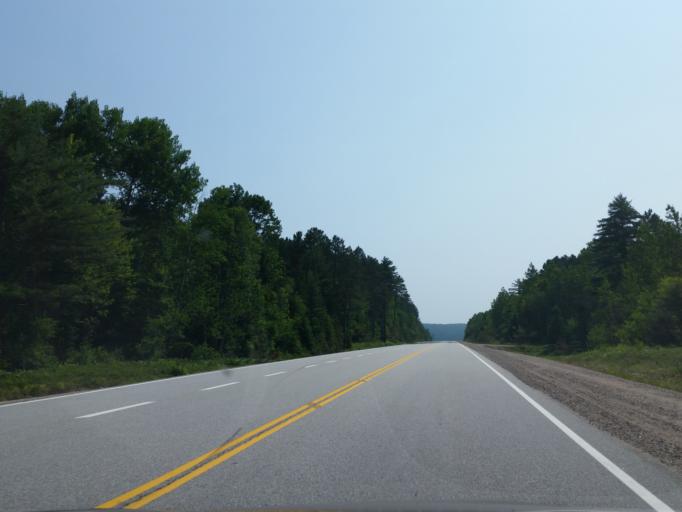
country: CA
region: Ontario
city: Mattawa
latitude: 46.2825
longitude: -78.4113
